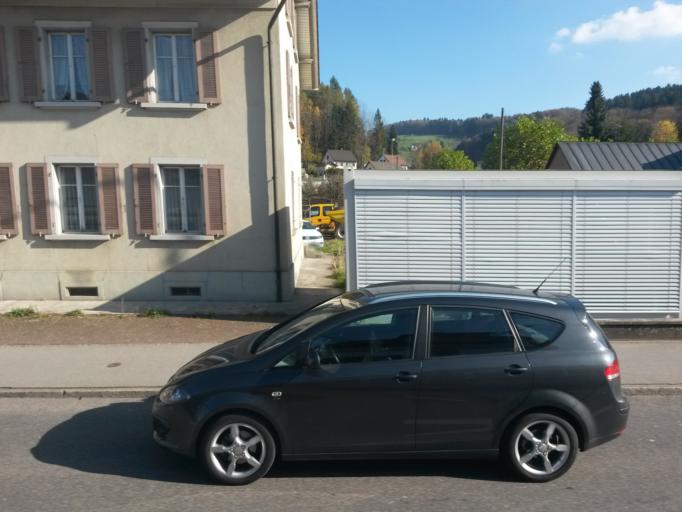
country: CH
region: Aargau
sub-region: Bezirk Kulm
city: Unterkulm
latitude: 47.3125
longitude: 8.1139
